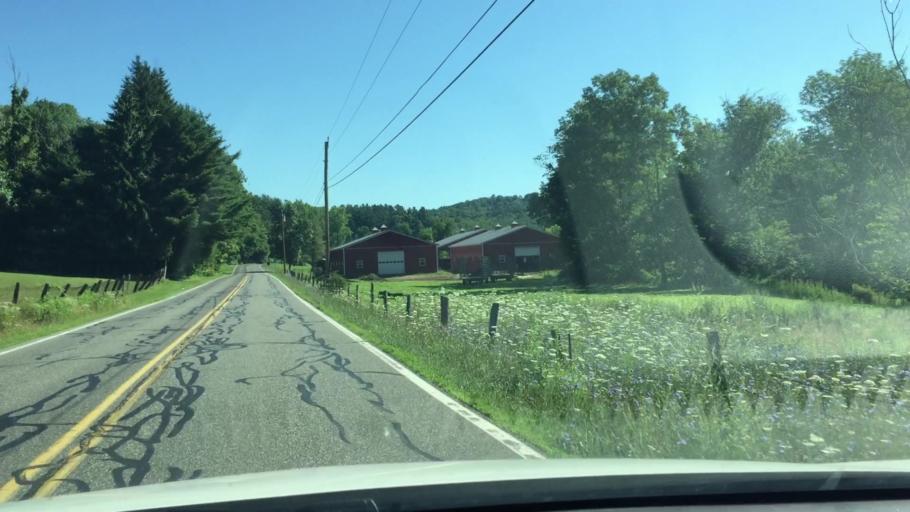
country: US
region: Massachusetts
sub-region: Berkshire County
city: West Stockbridge
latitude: 42.3503
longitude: -73.3628
